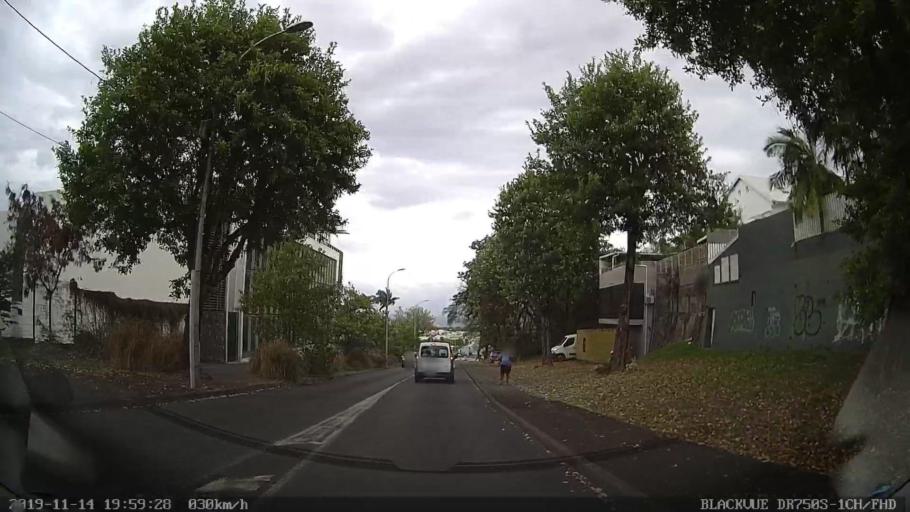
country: RE
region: Reunion
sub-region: Reunion
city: Saint-Denis
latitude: -20.9043
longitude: 55.4877
